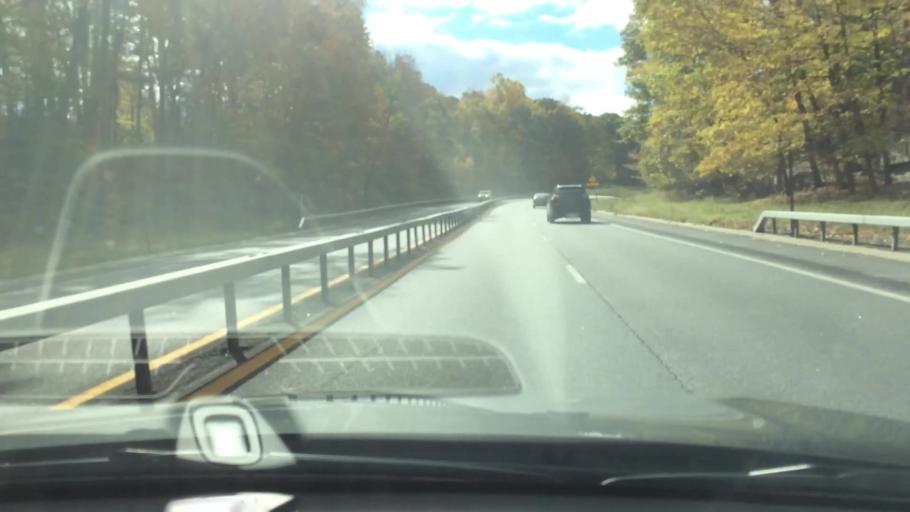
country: US
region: New York
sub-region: Dutchess County
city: Brinckerhoff
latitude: 41.4945
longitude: -73.8016
